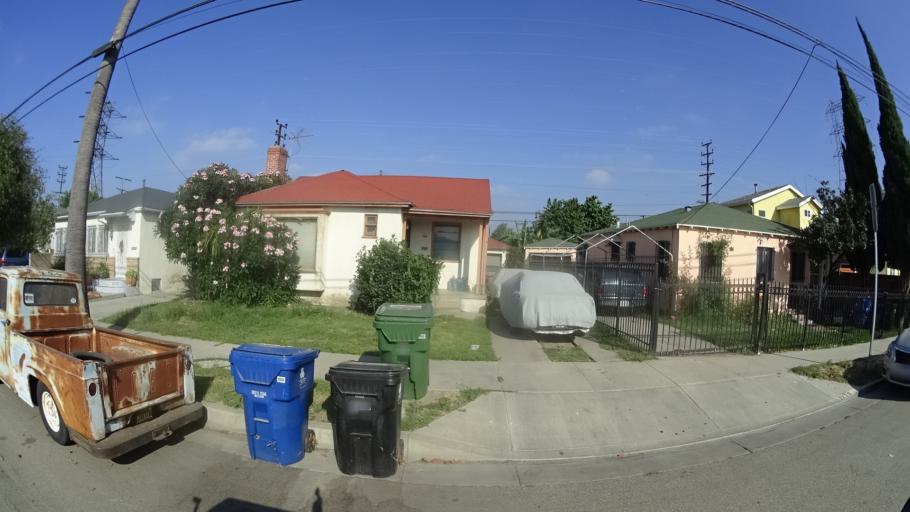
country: US
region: California
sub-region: Los Angeles County
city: Culver City
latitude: 34.0305
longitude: -118.3706
